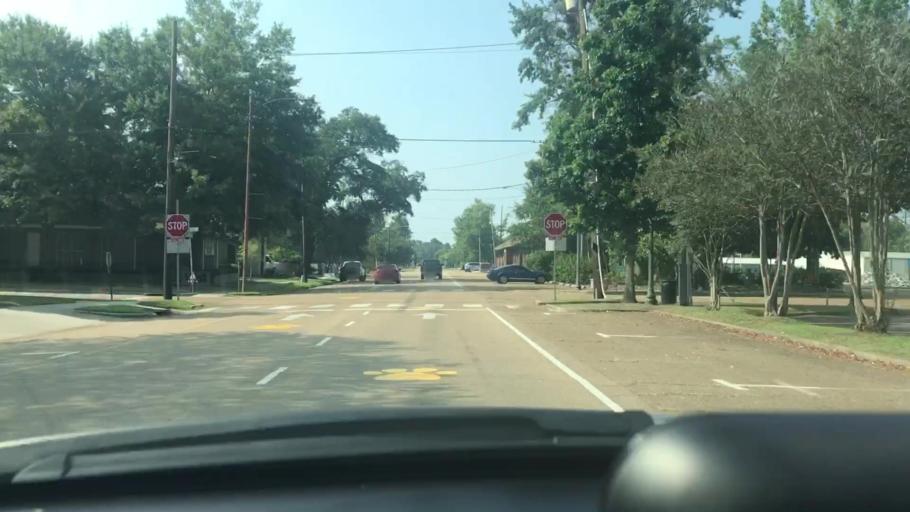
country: US
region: Louisiana
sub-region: Tangipahoa Parish
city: Hammond
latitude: 30.5054
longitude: -90.4618
